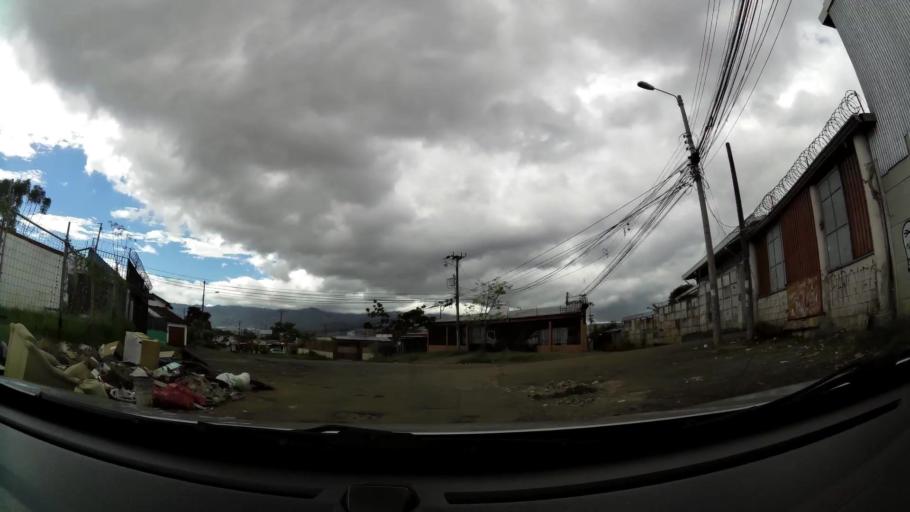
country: CR
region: San Jose
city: Curridabat
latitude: 9.9223
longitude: -84.0381
